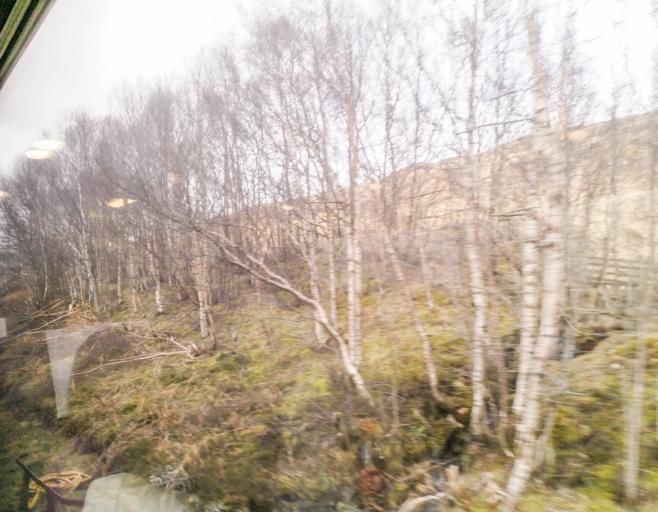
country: GB
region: Scotland
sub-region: Highland
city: Spean Bridge
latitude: 56.7845
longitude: -4.7321
